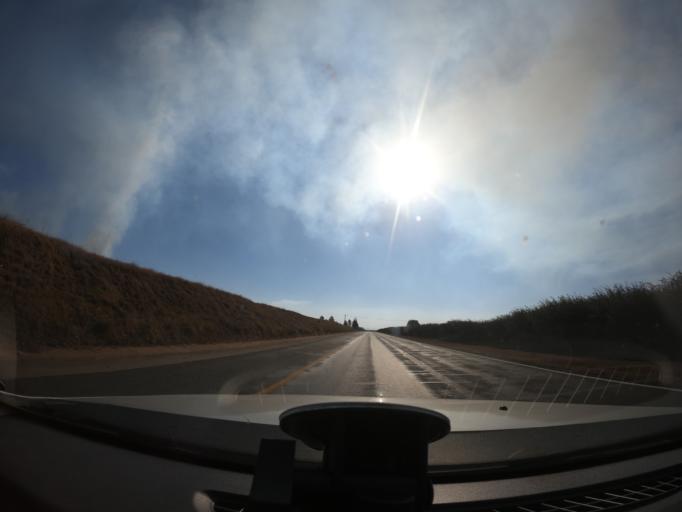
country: ZA
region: Gauteng
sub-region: Sedibeng District Municipality
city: Heidelberg
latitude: -26.4539
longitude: 28.3229
